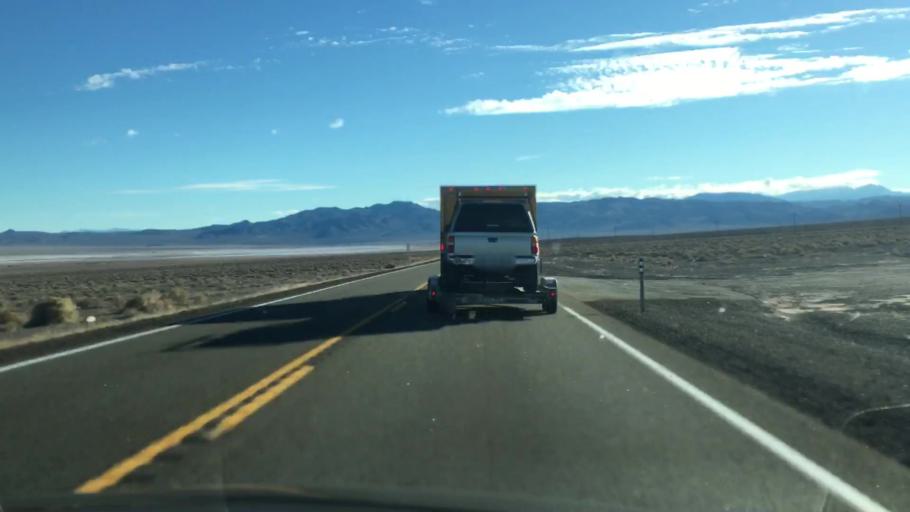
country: US
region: Nevada
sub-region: Mineral County
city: Hawthorne
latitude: 38.3372
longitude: -118.1031
